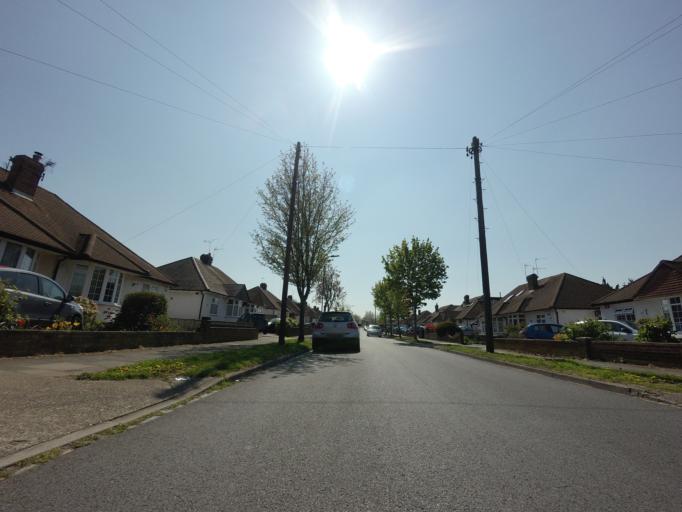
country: GB
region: England
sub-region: Greater London
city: Orpington
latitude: 51.3793
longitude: 0.1103
